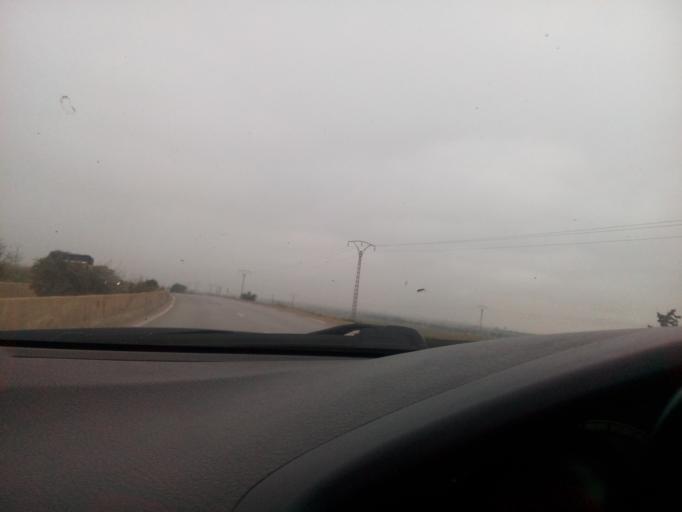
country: DZ
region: Oran
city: Bou Tlelis
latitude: 35.5585
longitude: -0.9336
